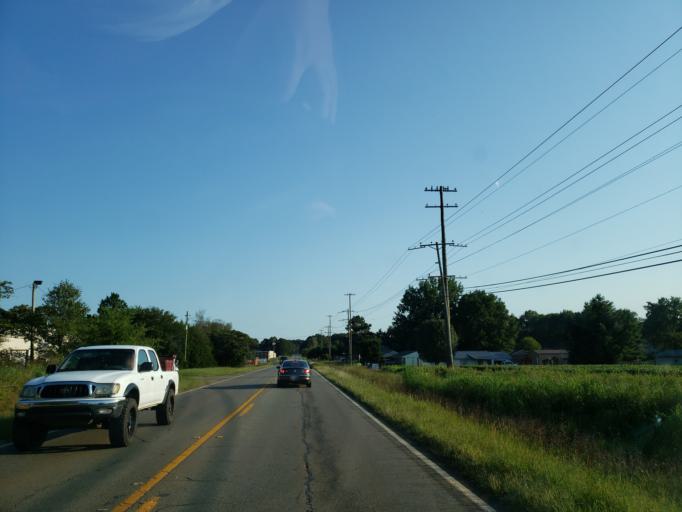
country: US
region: Georgia
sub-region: Murray County
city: Chatsworth
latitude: 34.7471
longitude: -84.8202
